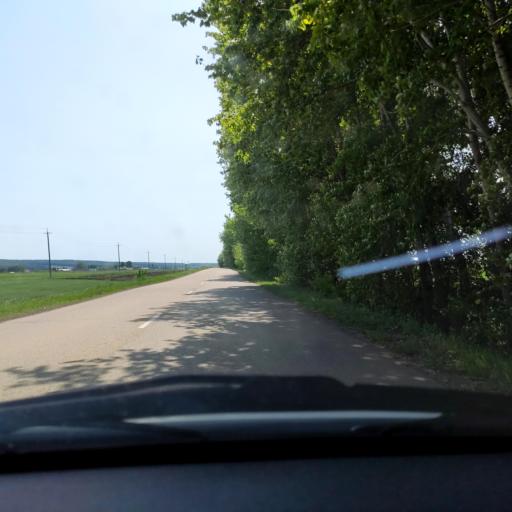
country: RU
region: Bashkortostan
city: Avdon
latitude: 54.5109
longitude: 55.6249
